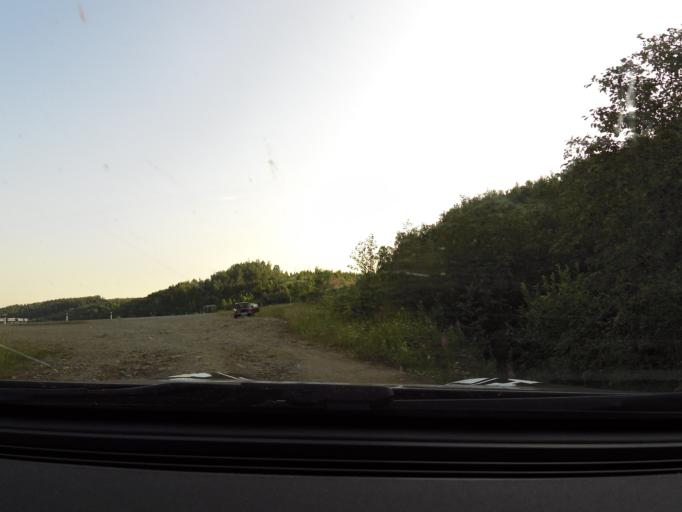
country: RU
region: Sverdlovsk
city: Mikhaylovsk
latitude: 56.4246
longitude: 59.0629
